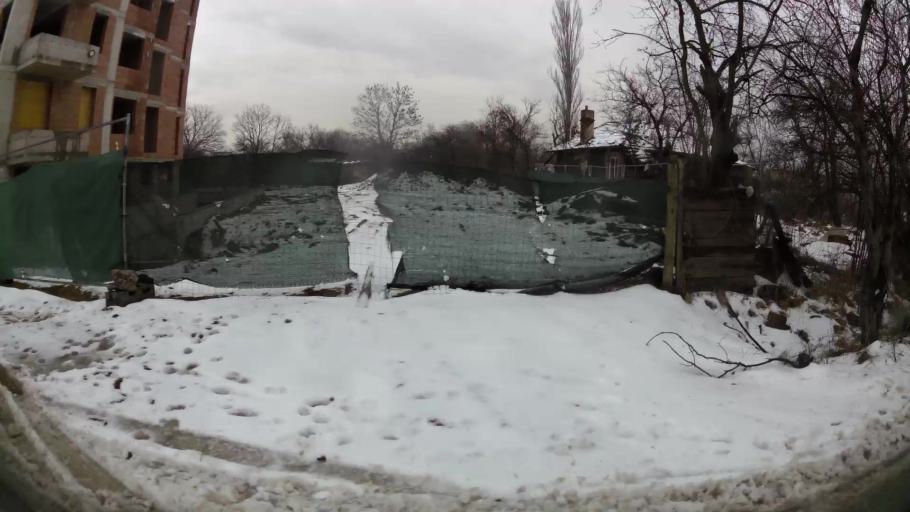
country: BG
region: Sofia-Capital
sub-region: Stolichna Obshtina
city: Sofia
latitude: 42.6555
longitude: 23.3002
